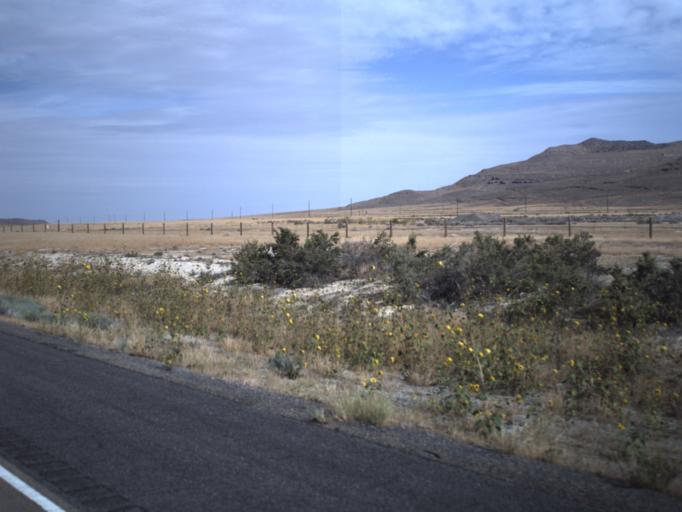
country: US
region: Utah
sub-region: Tooele County
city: Grantsville
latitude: 40.7890
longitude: -112.8289
